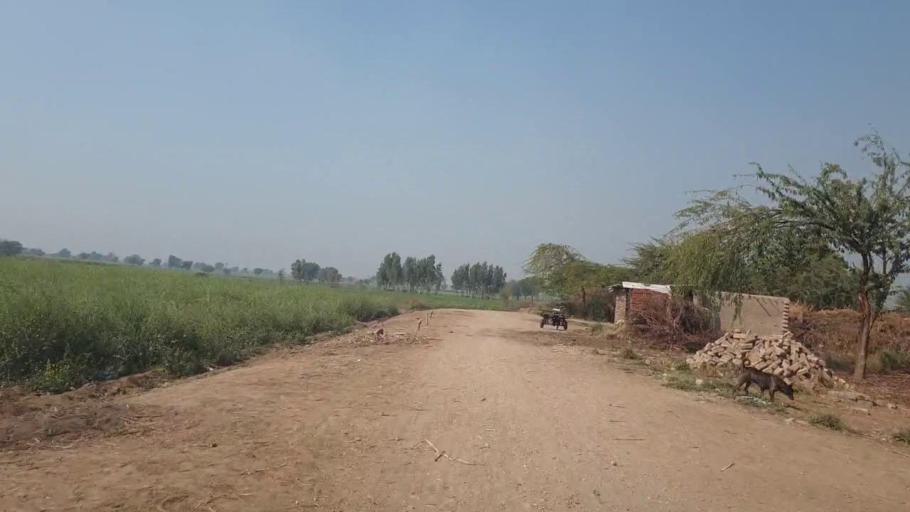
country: PK
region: Sindh
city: Tando Allahyar
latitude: 25.6109
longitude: 68.7350
